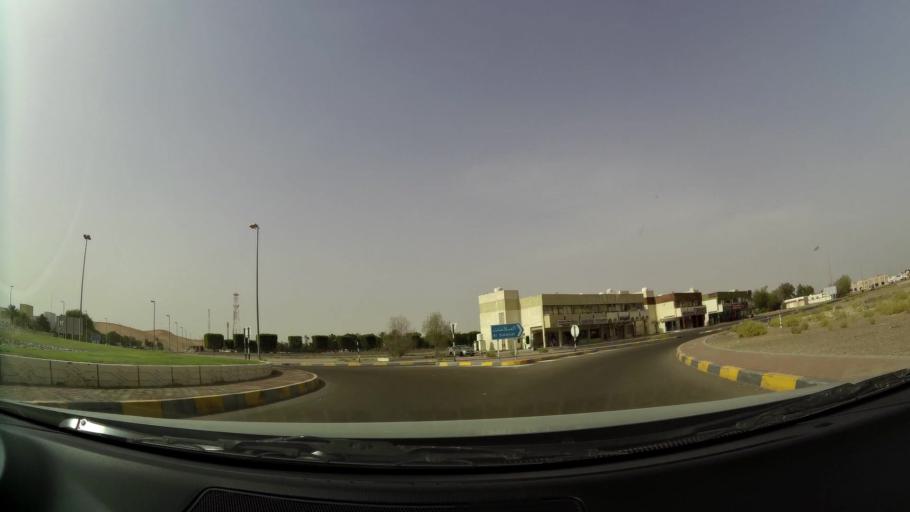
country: AE
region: Abu Dhabi
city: Al Ain
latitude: 24.2033
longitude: 55.5783
